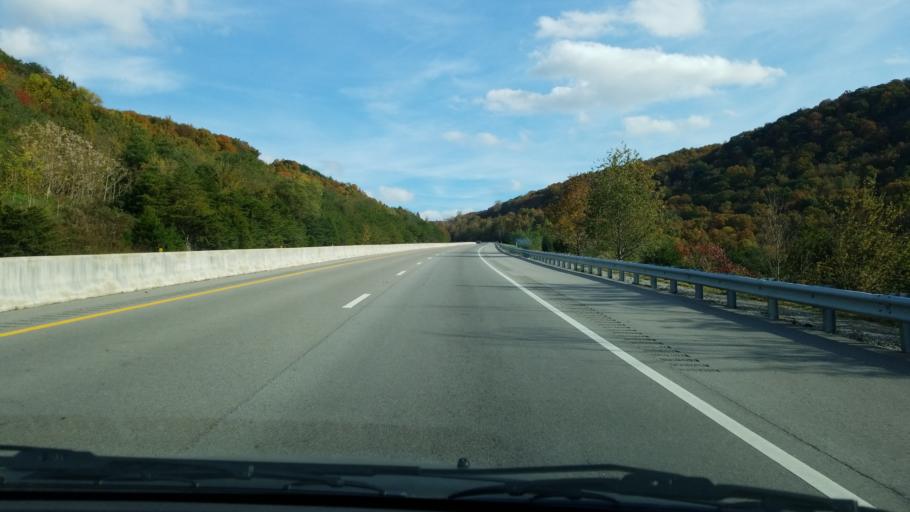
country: US
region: Tennessee
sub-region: Sequatchie County
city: Dunlap
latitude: 35.3609
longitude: -85.3223
